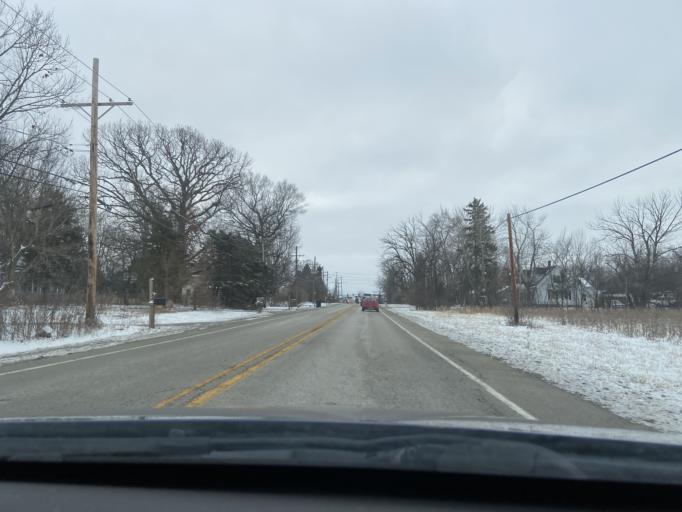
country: US
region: Illinois
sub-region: Lake County
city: Round Lake Park
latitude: 42.3599
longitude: -88.0680
